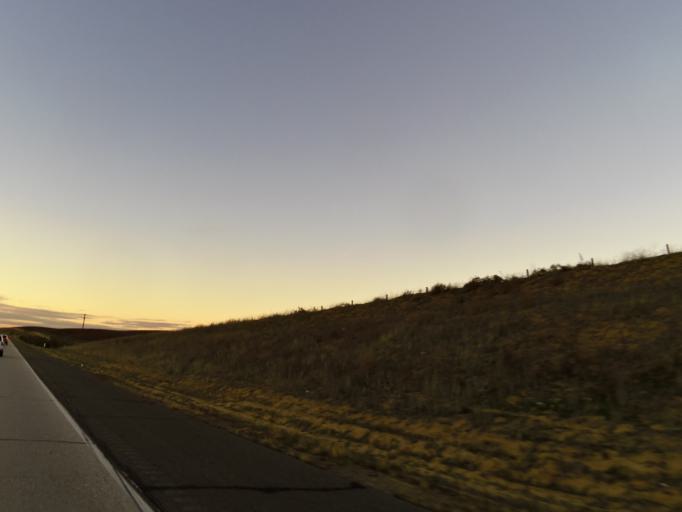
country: US
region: California
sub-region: Monterey County
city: King City
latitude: 36.0678
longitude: -120.9862
